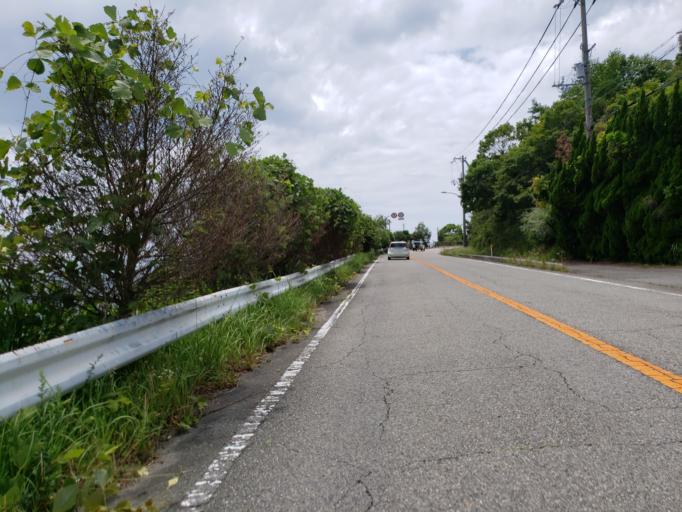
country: JP
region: Hyogo
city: Aioi
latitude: 34.7784
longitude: 134.5223
